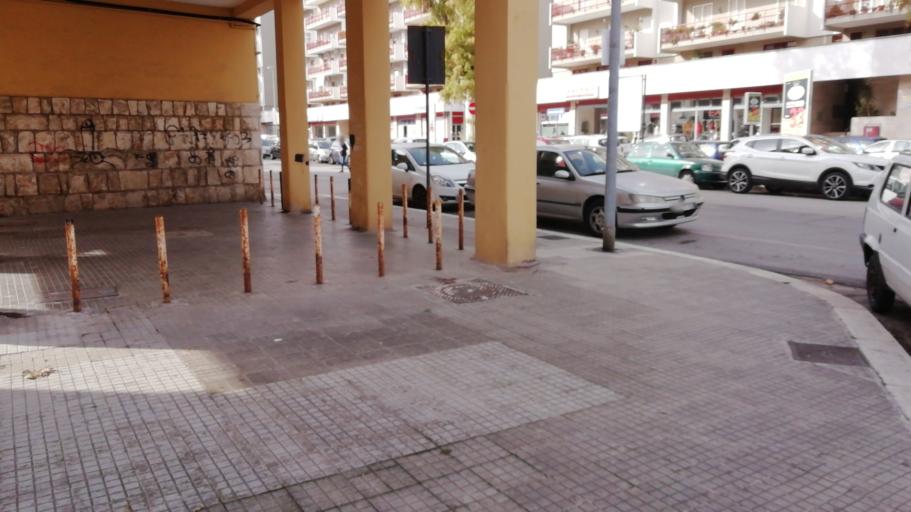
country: IT
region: Apulia
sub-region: Provincia di Bari
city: Bari
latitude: 41.1145
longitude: 16.8938
